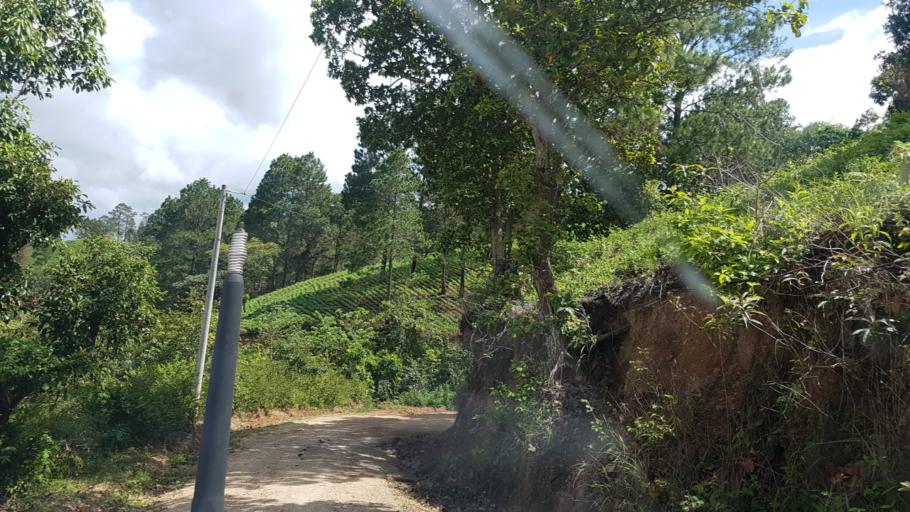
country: NI
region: Nueva Segovia
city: Ciudad Antigua
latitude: 13.6520
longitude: -86.2383
